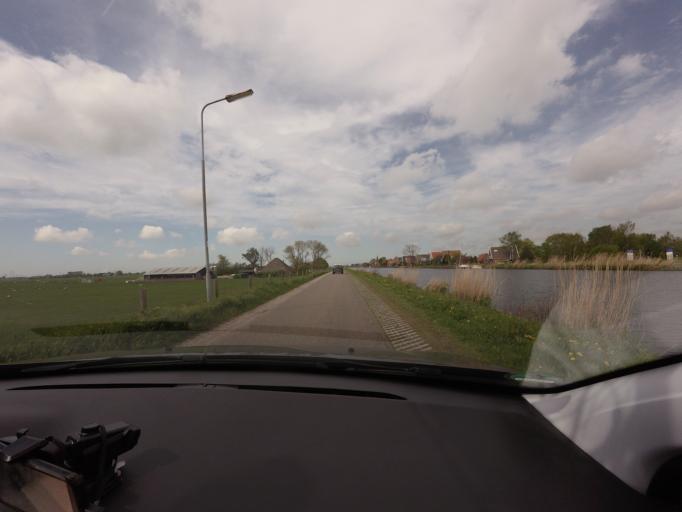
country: NL
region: North Holland
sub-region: Gemeente Zaanstad
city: Zaanstad
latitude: 52.5435
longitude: 4.8202
